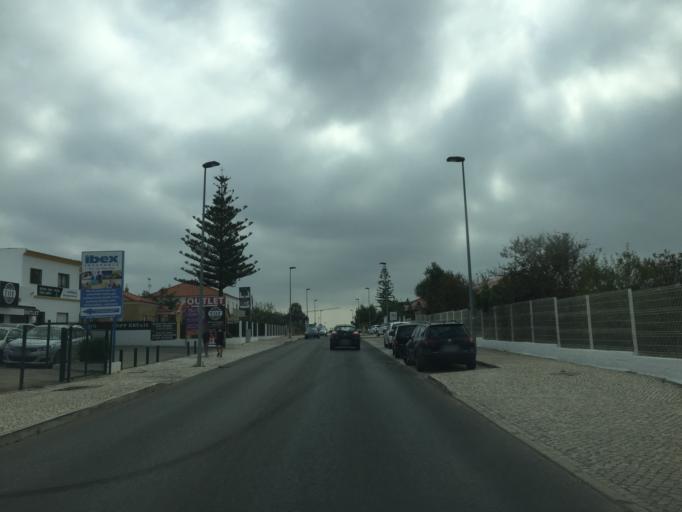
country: PT
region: Faro
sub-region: Loule
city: Almancil
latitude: 37.0843
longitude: -8.0211
